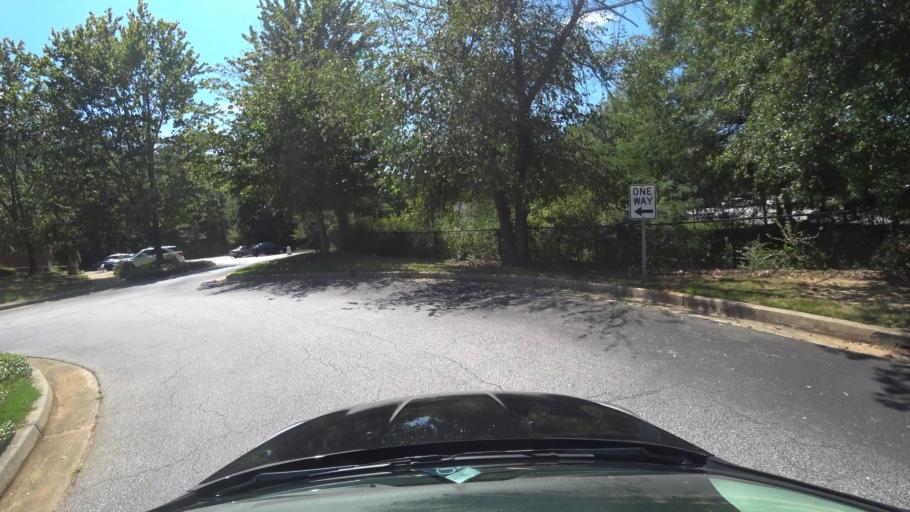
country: US
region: Georgia
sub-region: Newton County
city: Covington
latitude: 33.5997
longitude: -83.8397
